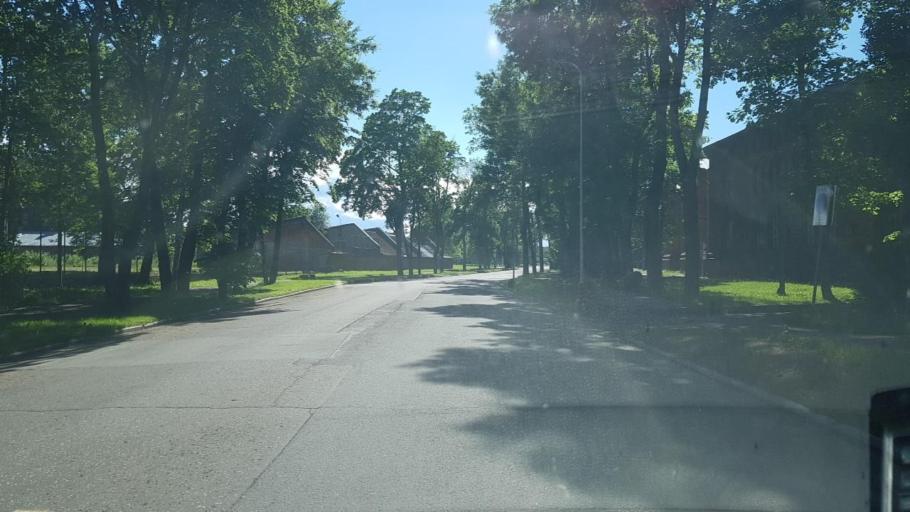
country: EE
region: Ida-Virumaa
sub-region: Narva linn
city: Narva
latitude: 59.3602
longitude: 28.1934
